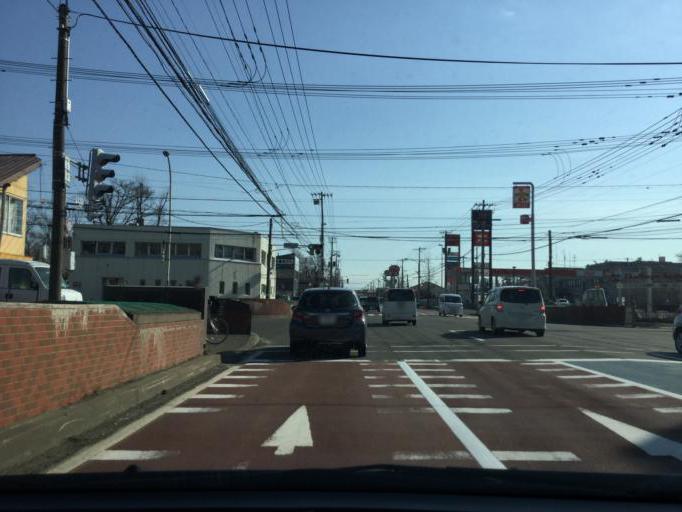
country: JP
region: Hokkaido
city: Iwamizawa
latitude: 43.1976
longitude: 141.7717
